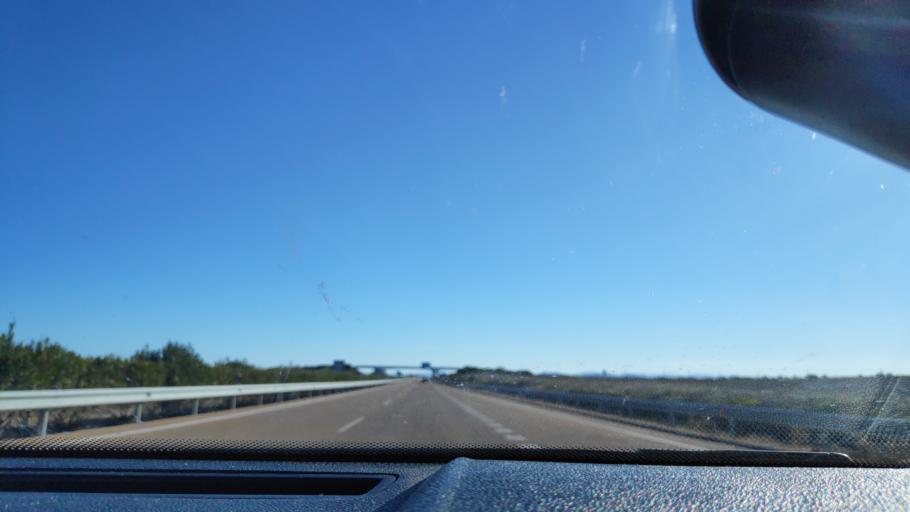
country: ES
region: Extremadura
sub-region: Provincia de Badajoz
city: Los Santos de Maimona
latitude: 38.4151
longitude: -6.3438
